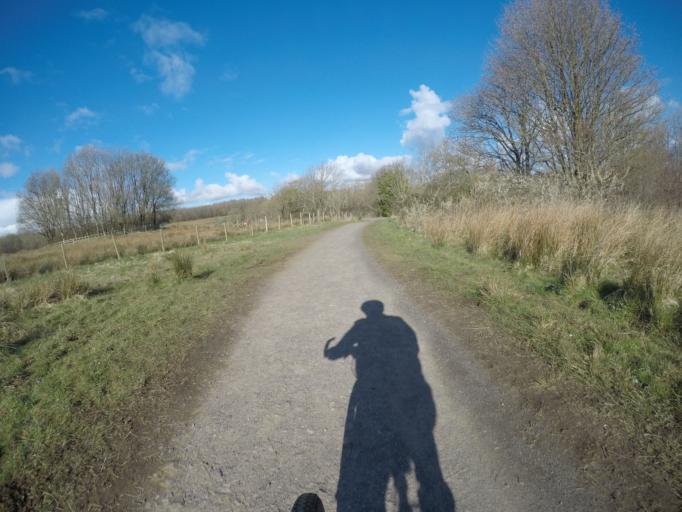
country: GB
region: Scotland
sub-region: North Ayrshire
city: Irvine
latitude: 55.6427
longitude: -4.6601
